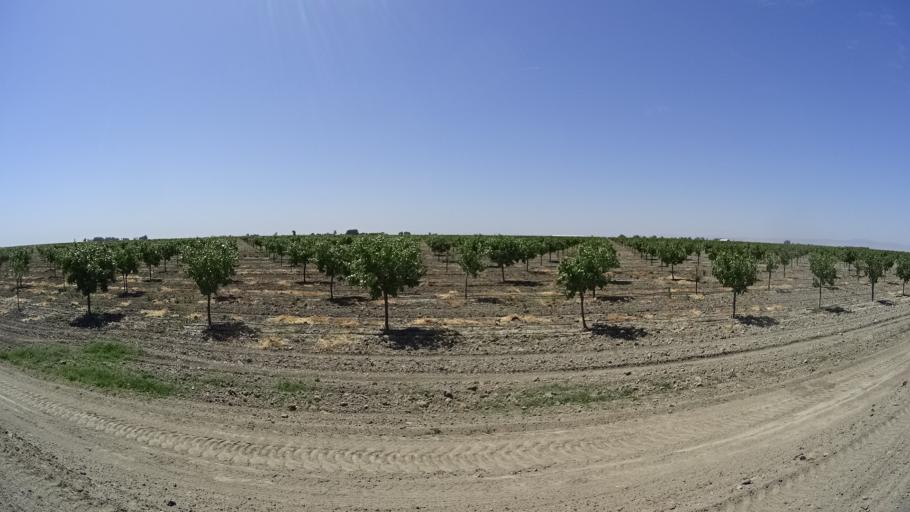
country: US
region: California
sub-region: Kings County
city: Stratford
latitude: 36.1894
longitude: -119.7862
